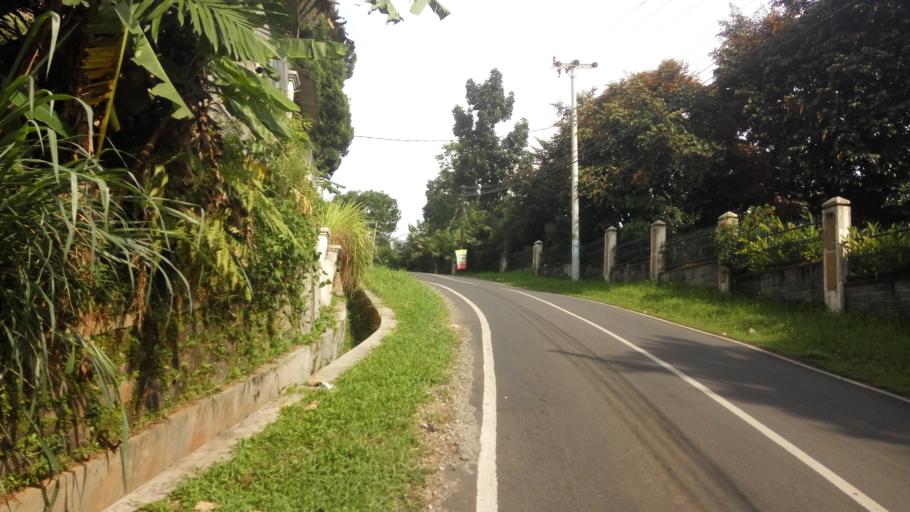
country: ID
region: Central Java
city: Ungaran
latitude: -7.1441
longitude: 110.4176
